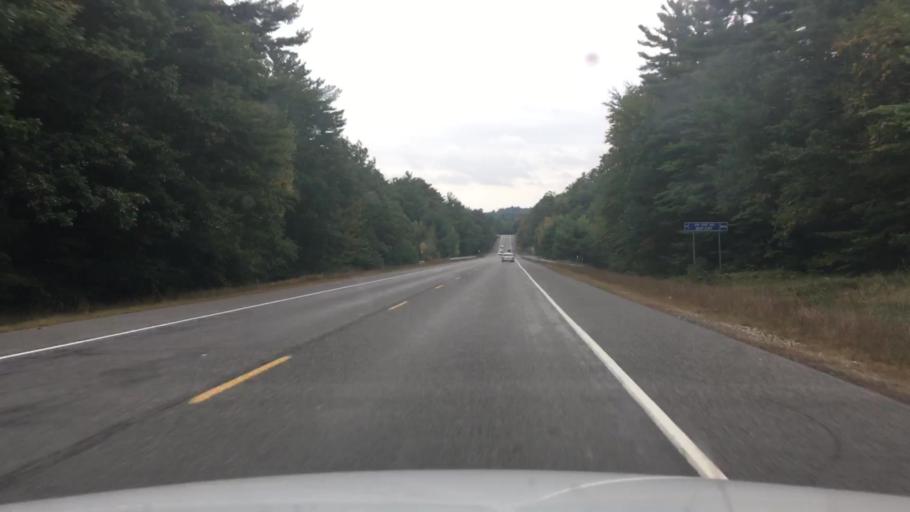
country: US
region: New Hampshire
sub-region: Carroll County
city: Wolfeboro
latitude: 43.5006
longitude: -71.2622
